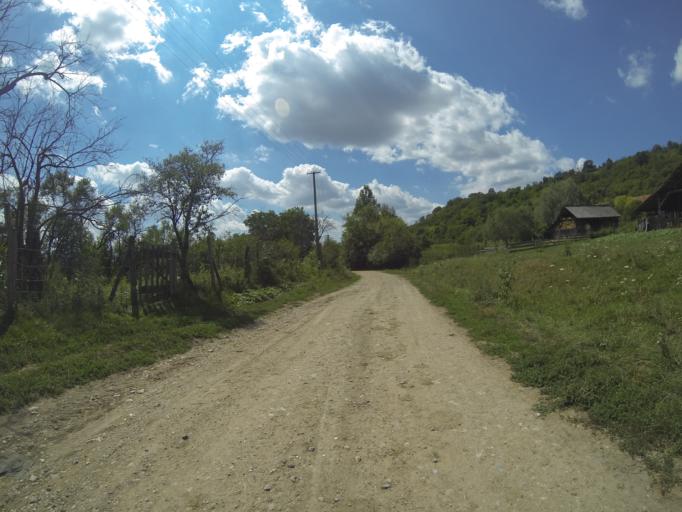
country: RO
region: Brasov
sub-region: Comuna Mandra
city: Mandra
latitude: 45.8529
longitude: 25.0538
